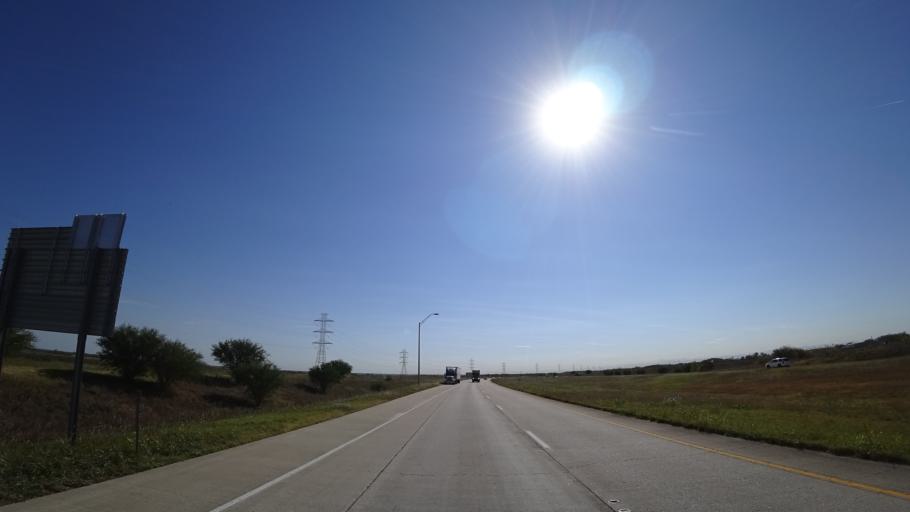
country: US
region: Texas
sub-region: Travis County
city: Pflugerville
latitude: 30.3965
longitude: -97.5799
